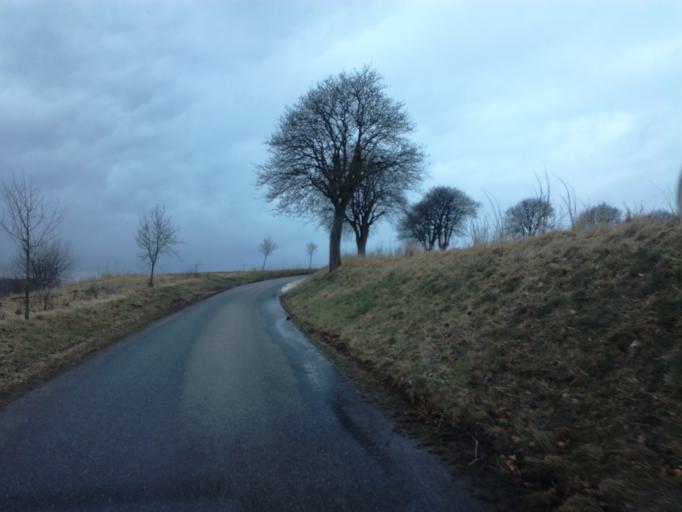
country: DK
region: South Denmark
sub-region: Vejle Kommune
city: Brejning
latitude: 55.6220
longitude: 9.7115
